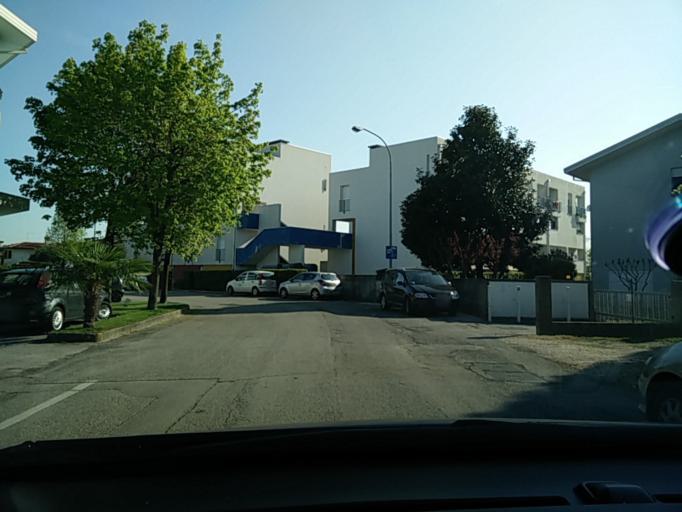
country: IT
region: Veneto
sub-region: Provincia di Venezia
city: Musile di Piave
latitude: 45.6190
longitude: 12.5576
